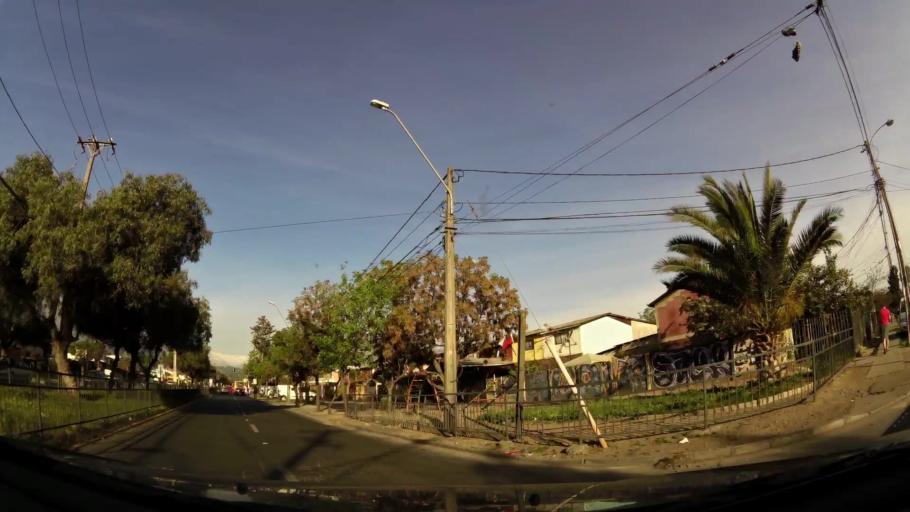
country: CL
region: Santiago Metropolitan
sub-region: Provincia de Cordillera
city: Puente Alto
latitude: -33.5972
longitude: -70.5675
